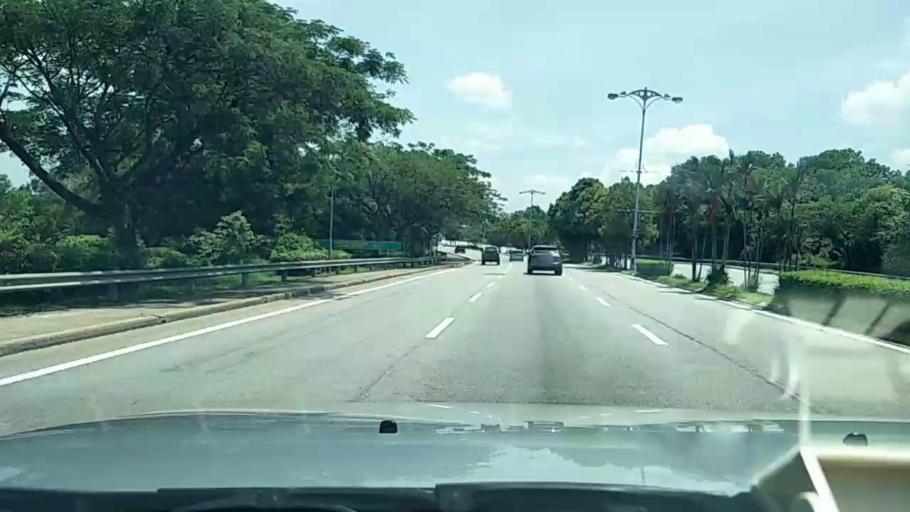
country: MY
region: Putrajaya
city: Putrajaya
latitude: 2.9456
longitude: 101.6696
